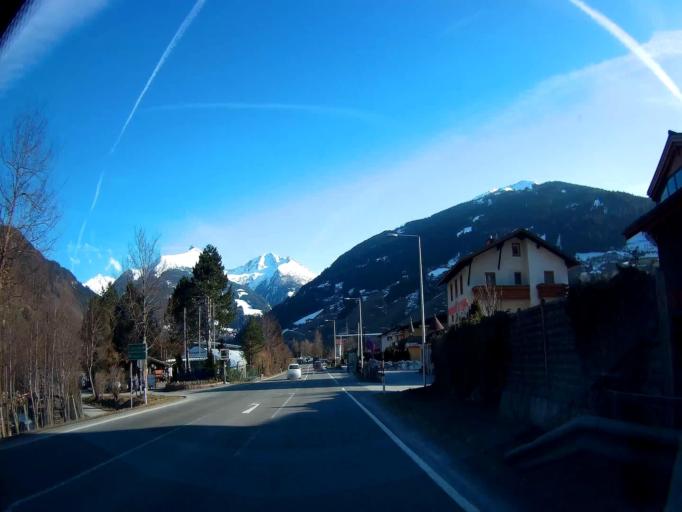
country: AT
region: Salzburg
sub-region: Politischer Bezirk Sankt Johann im Pongau
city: Bad Hofgastein
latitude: 47.1518
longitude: 13.1127
